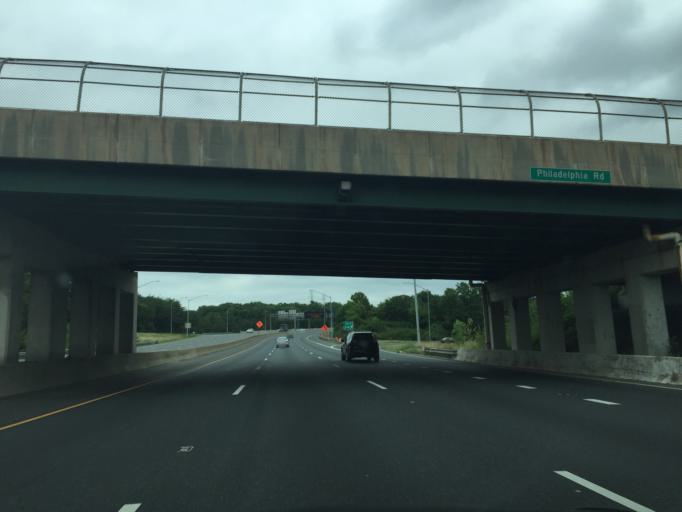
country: US
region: Maryland
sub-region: Baltimore County
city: Rossville
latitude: 39.3358
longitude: -76.4914
